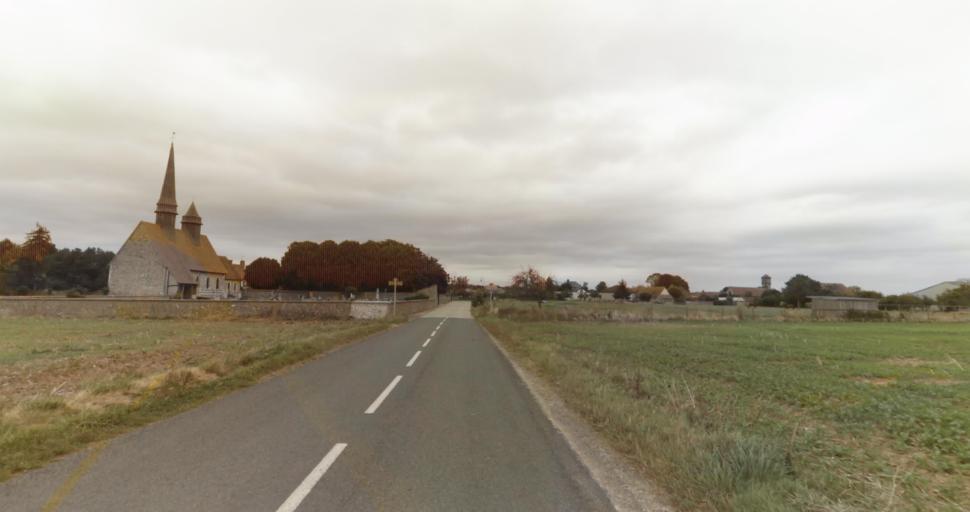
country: FR
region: Haute-Normandie
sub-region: Departement de l'Eure
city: La Couture-Boussey
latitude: 48.9347
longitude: 1.3936
